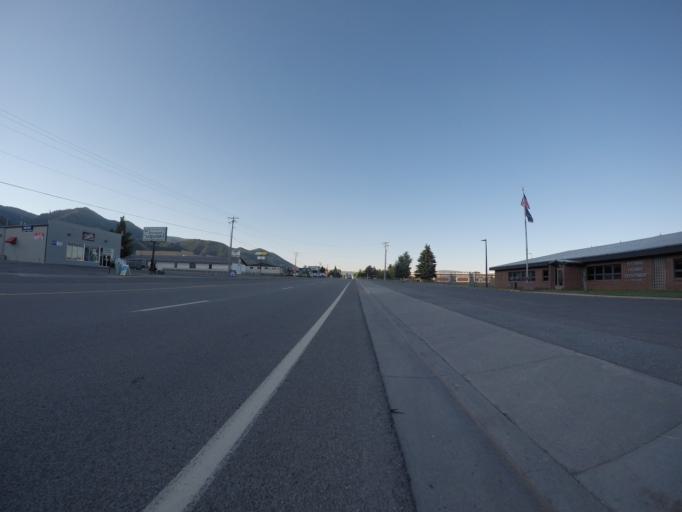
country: US
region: Wyoming
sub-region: Lincoln County
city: Afton
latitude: 42.7377
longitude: -110.9334
